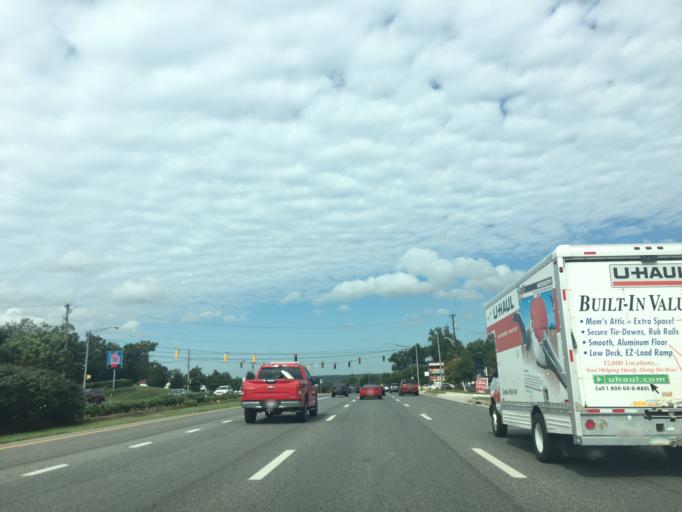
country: US
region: Maryland
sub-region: Anne Arundel County
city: Maryland City
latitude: 39.1001
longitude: -76.8149
